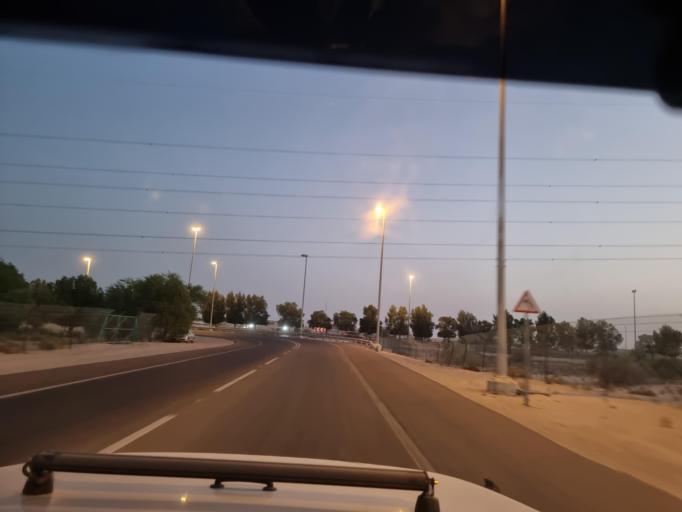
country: AE
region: Abu Dhabi
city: Abu Dhabi
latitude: 24.1939
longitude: 54.9898
